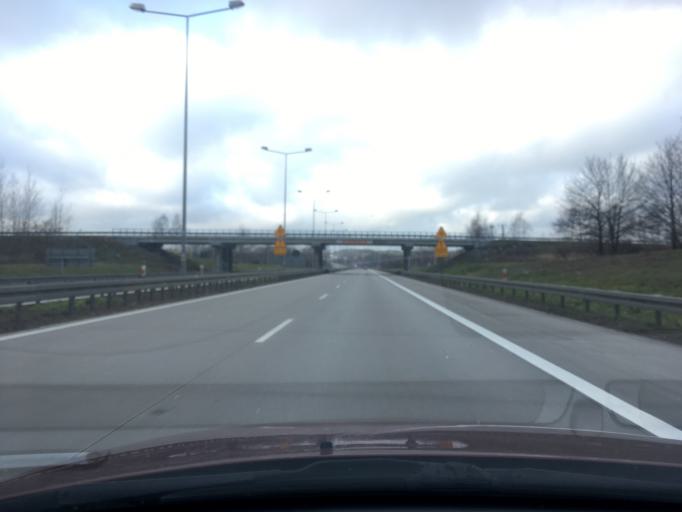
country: PL
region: Lower Silesian Voivodeship
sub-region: Powiat zgorzelecki
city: Zgorzelec
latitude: 51.1785
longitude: 15.0143
